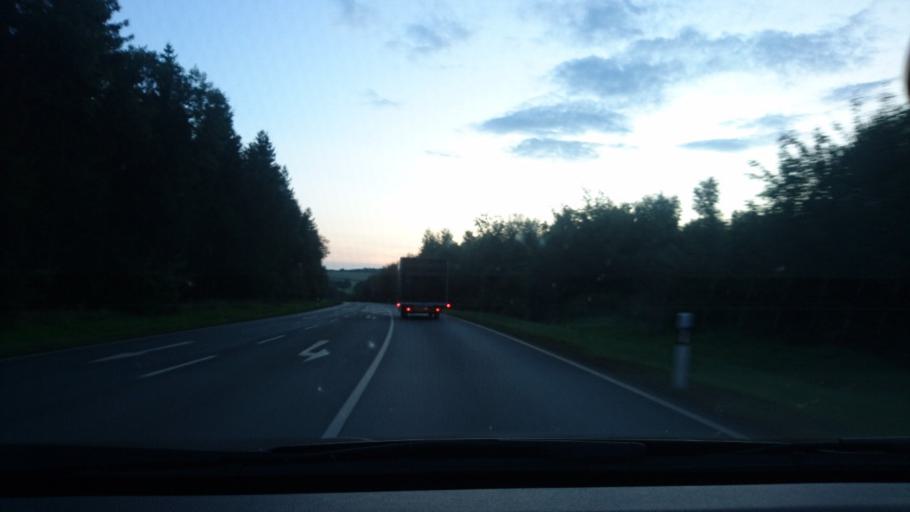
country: DE
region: Bavaria
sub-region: Upper Franconia
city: Koditz
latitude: 50.3444
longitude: 11.8251
